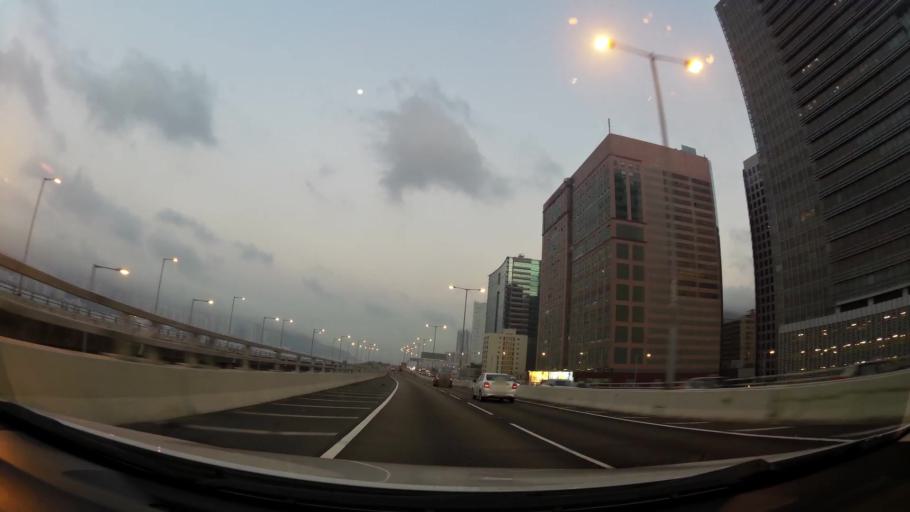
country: HK
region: Kowloon City
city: Kowloon
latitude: 22.2939
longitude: 114.2056
